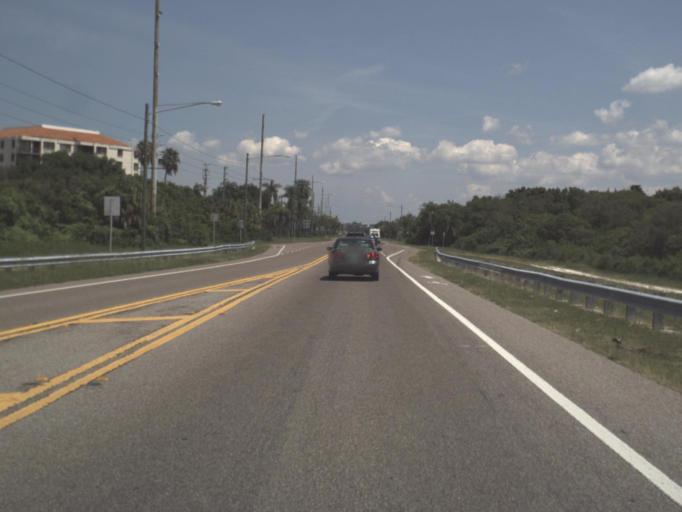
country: US
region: Florida
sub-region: Pinellas County
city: Tierra Verde
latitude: 27.7037
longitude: -82.7135
